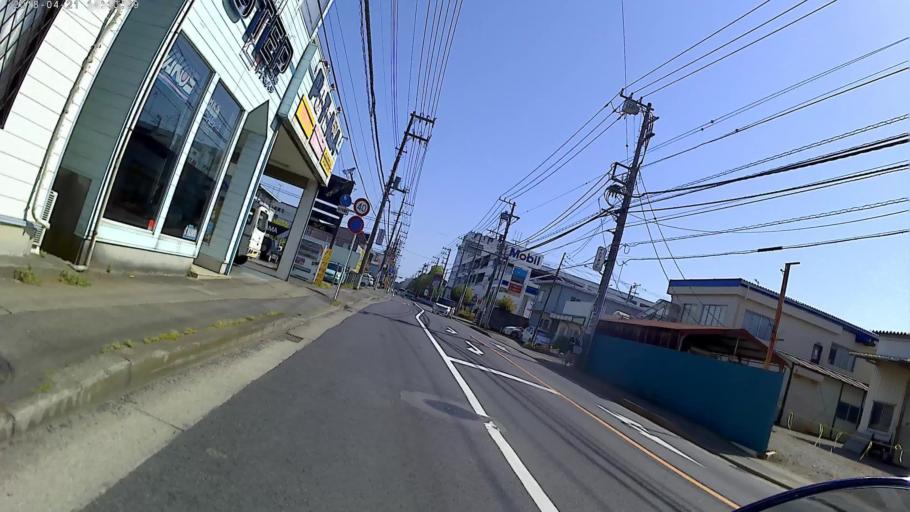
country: JP
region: Kanagawa
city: Hiratsuka
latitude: 35.3528
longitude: 139.3430
